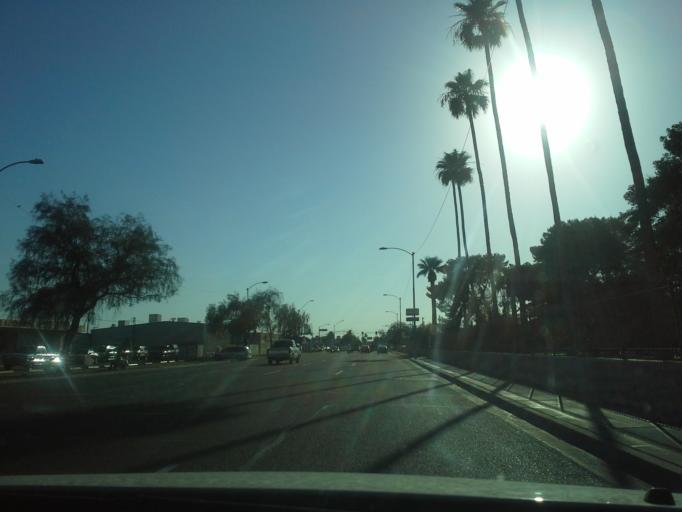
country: US
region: Arizona
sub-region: Maricopa County
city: Phoenix
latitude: 33.4513
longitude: -112.1108
